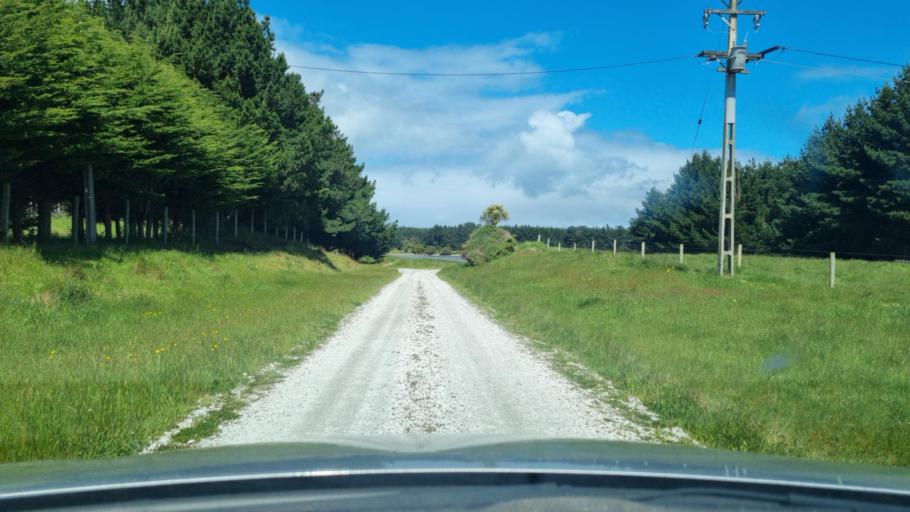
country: NZ
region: Southland
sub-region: Invercargill City
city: Invercargill
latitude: -46.4580
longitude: 168.2709
